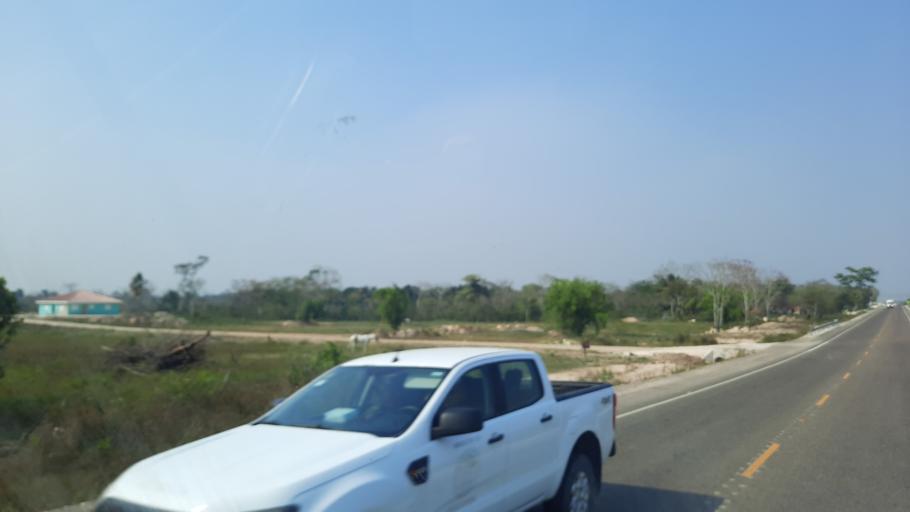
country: BZ
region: Cayo
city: Belmopan
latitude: 17.2395
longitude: -88.8291
